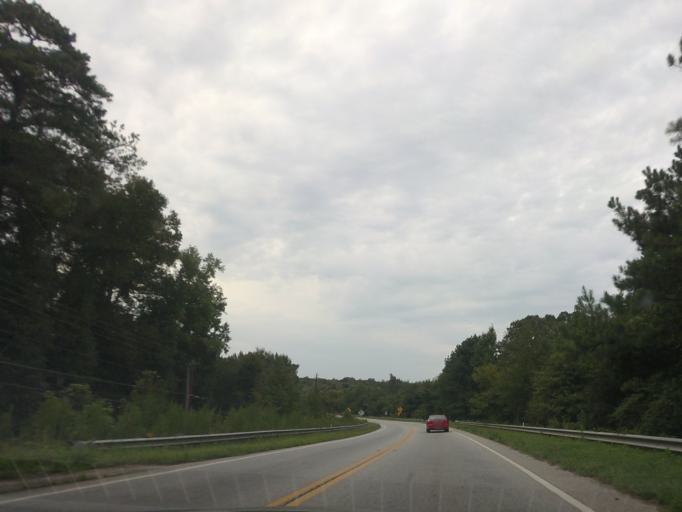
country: US
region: Georgia
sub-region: Bibb County
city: Macon
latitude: 32.8024
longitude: -83.5011
